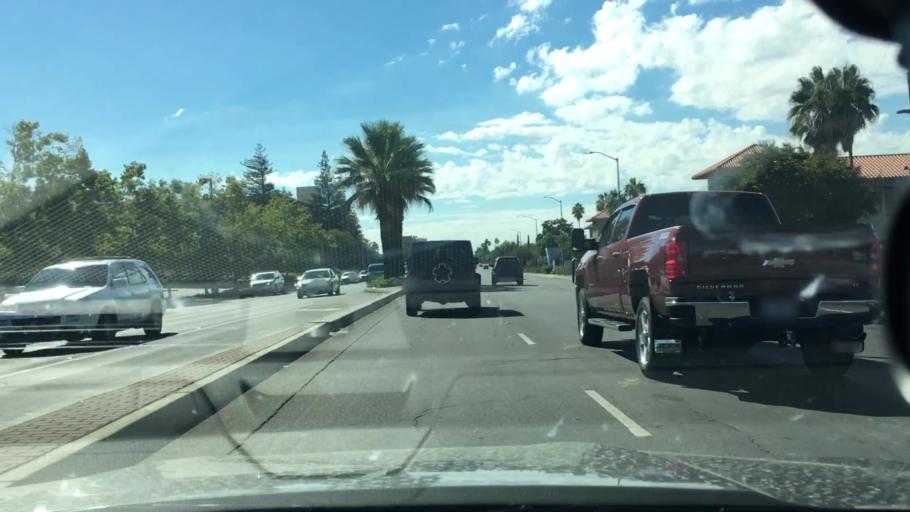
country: US
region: California
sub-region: Sacramento County
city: Arden-Arcade
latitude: 38.6173
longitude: -121.3830
